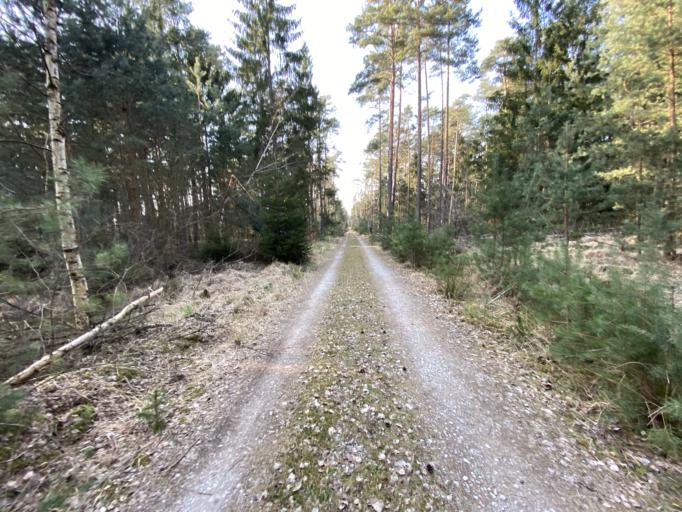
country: DE
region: Bavaria
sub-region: Regierungsbezirk Mittelfranken
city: Uttenreuth
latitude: 49.5497
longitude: 11.0712
